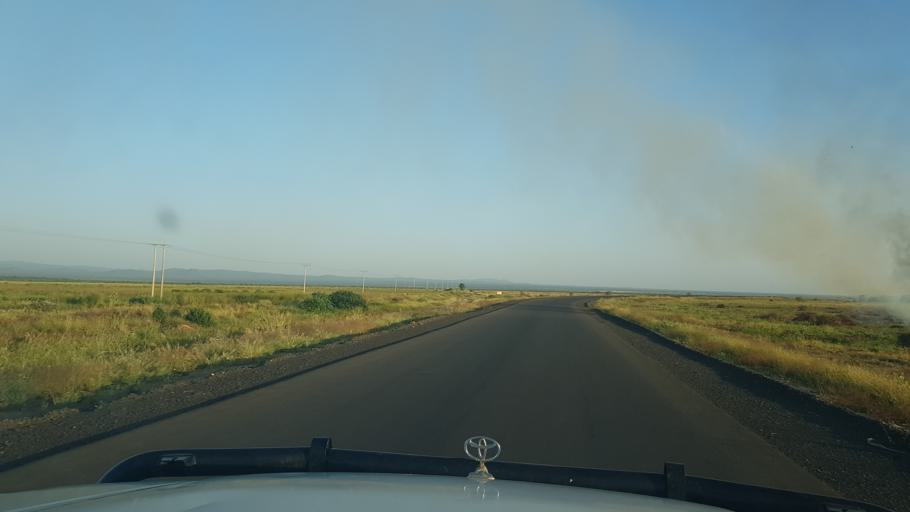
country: ET
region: Southern Nations, Nationalities, and People's Region
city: Lobuni
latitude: 5.1447
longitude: 36.1136
